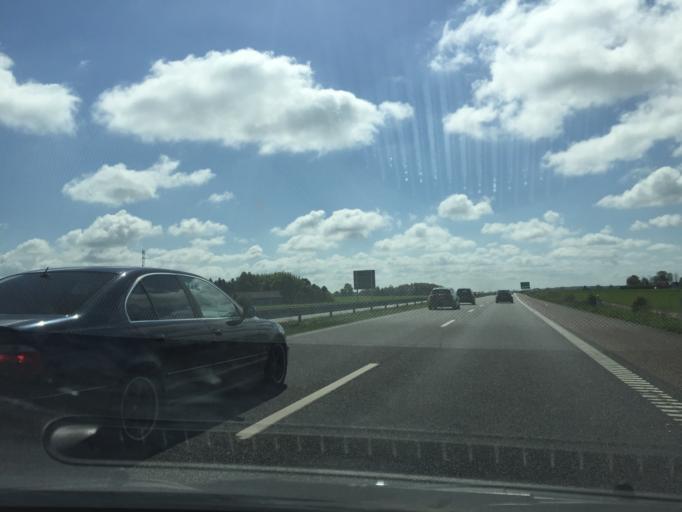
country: DK
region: Zealand
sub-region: Vordingborg Kommune
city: Nyrad
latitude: 54.9321
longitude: 11.9561
